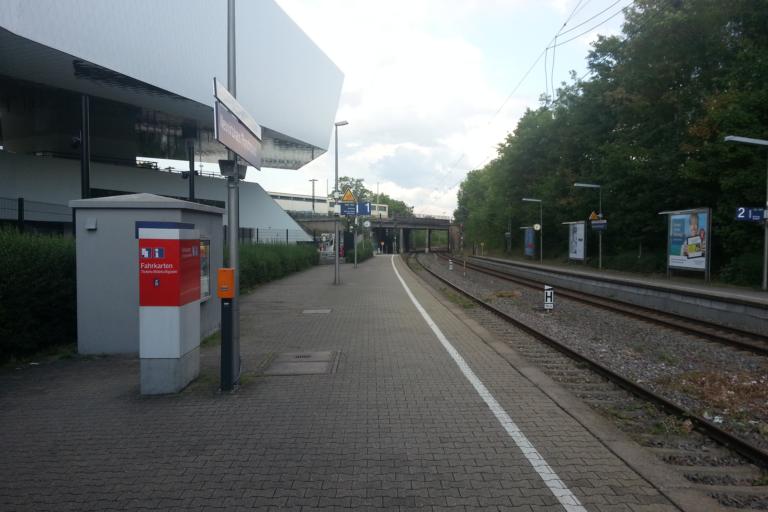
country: DE
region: Baden-Wuerttemberg
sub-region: Regierungsbezirk Stuttgart
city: Stuttgart Feuerbach
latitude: 48.8340
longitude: 9.1521
